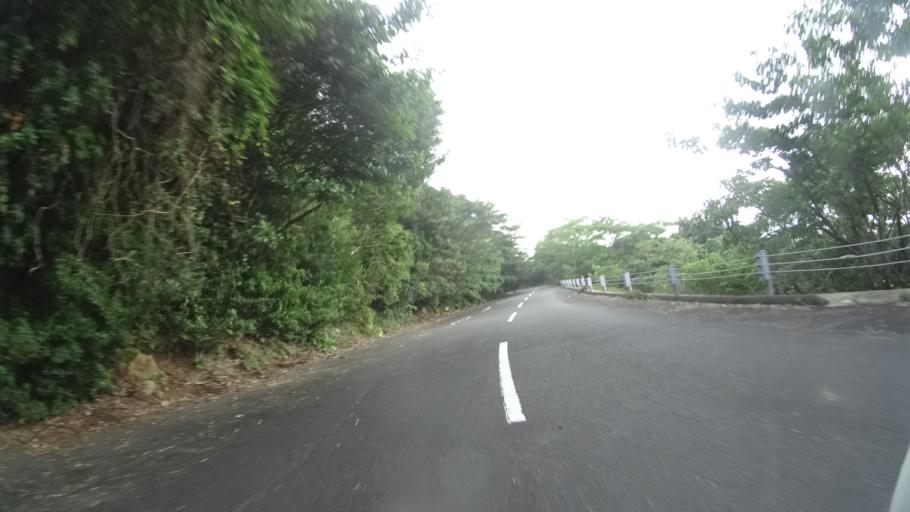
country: JP
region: Kagoshima
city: Nishinoomote
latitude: 30.3269
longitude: 130.3957
